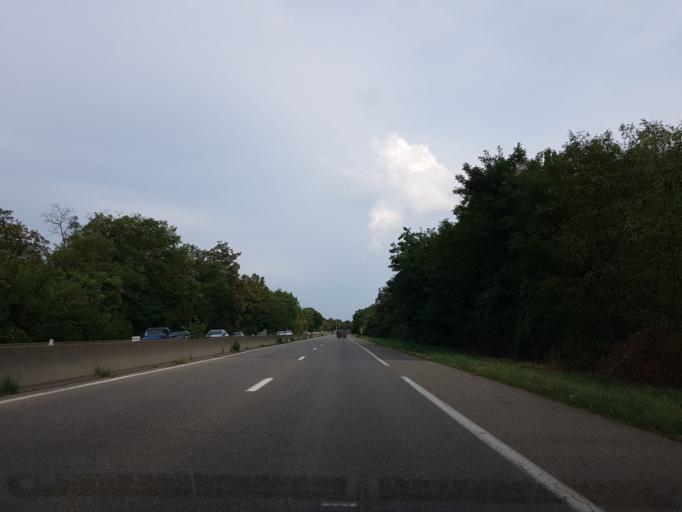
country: FR
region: Alsace
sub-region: Departement du Haut-Rhin
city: Kingersheim
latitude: 47.7850
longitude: 7.3217
